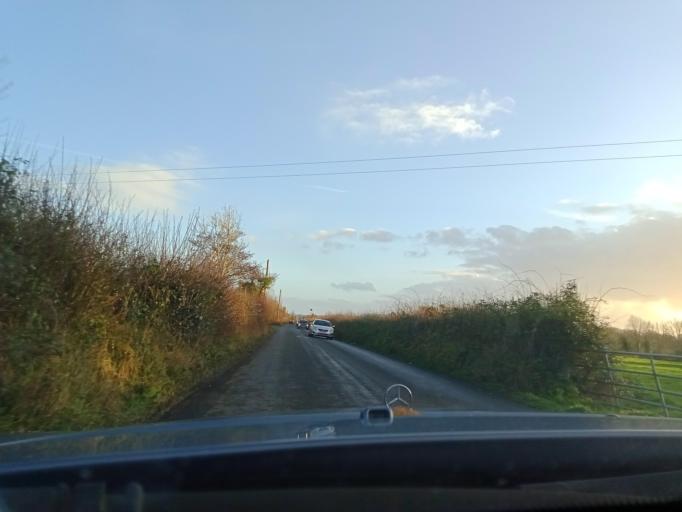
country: IE
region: Leinster
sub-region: Kilkenny
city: Callan
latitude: 52.5031
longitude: -7.3440
